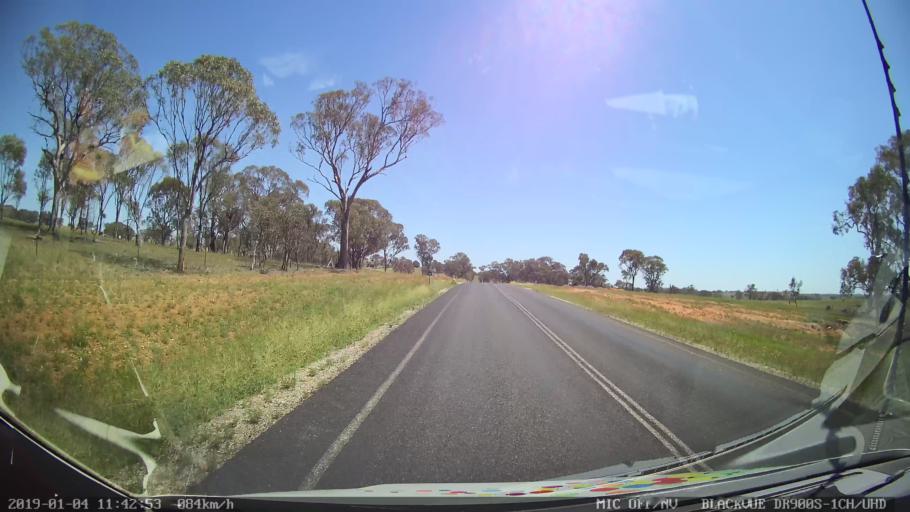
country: AU
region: New South Wales
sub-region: Cabonne
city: Molong
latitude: -32.9760
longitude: 148.7852
